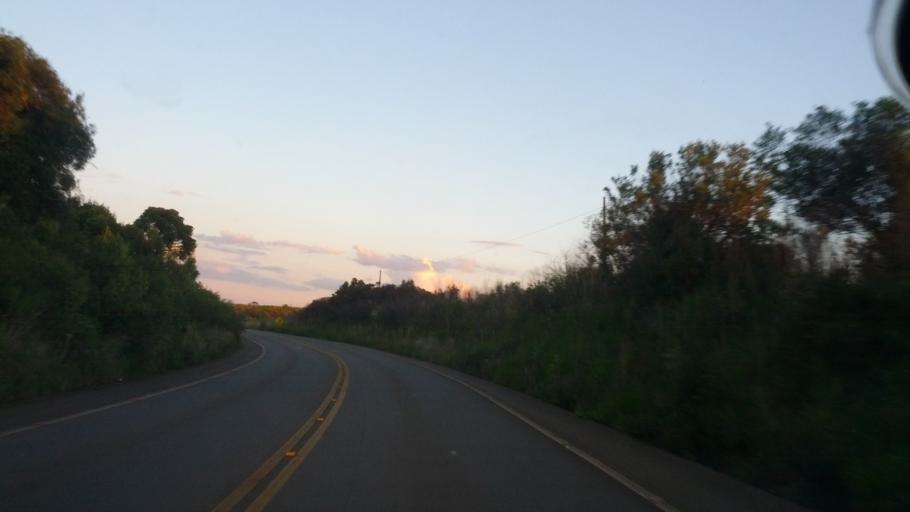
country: BR
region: Rio Grande do Sul
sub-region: Vacaria
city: Estrela
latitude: -27.8492
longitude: -50.8272
